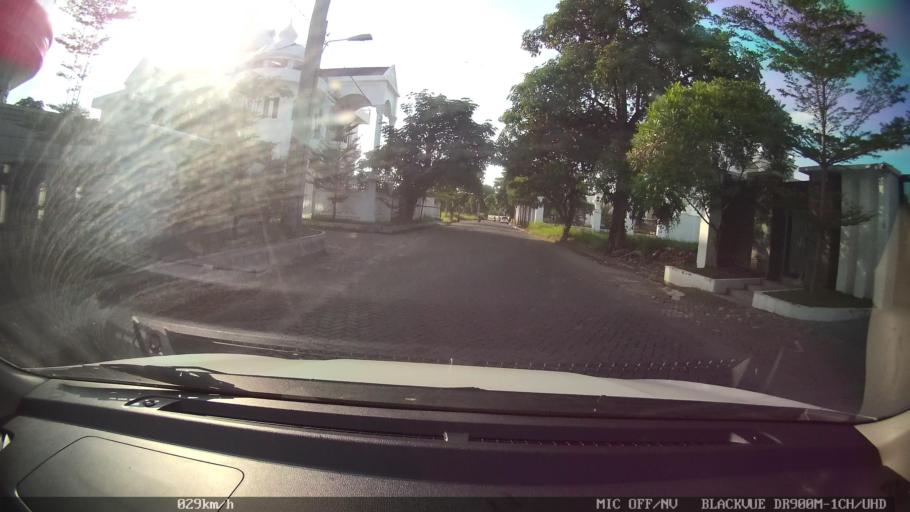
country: ID
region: North Sumatra
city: Medan
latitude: 3.6212
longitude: 98.6502
